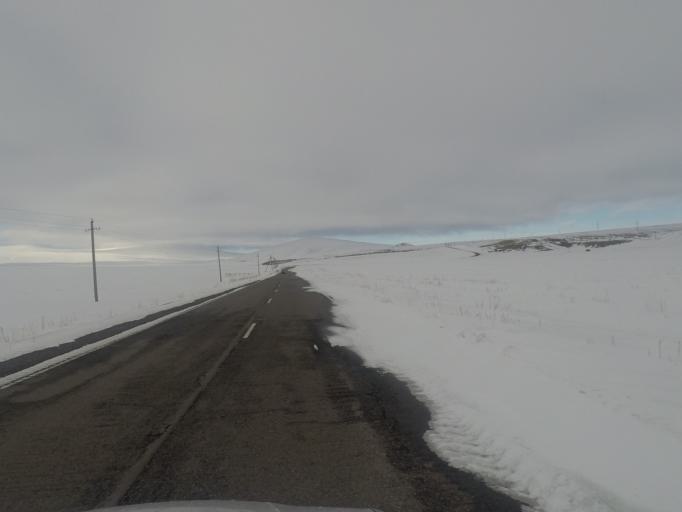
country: GE
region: Samtskhe-Javakheti
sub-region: Ninotsminda
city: Ninotsminda
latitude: 41.4301
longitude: 43.8373
